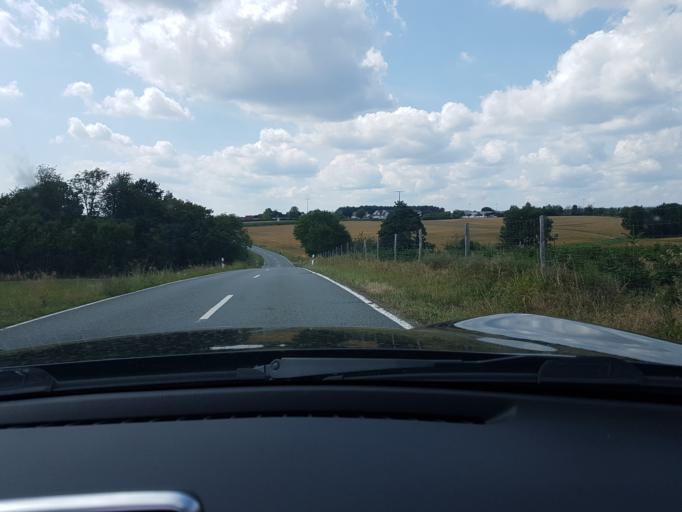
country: DE
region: Baden-Wuerttemberg
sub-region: Karlsruhe Region
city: Limbach
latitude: 49.4267
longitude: 9.2150
